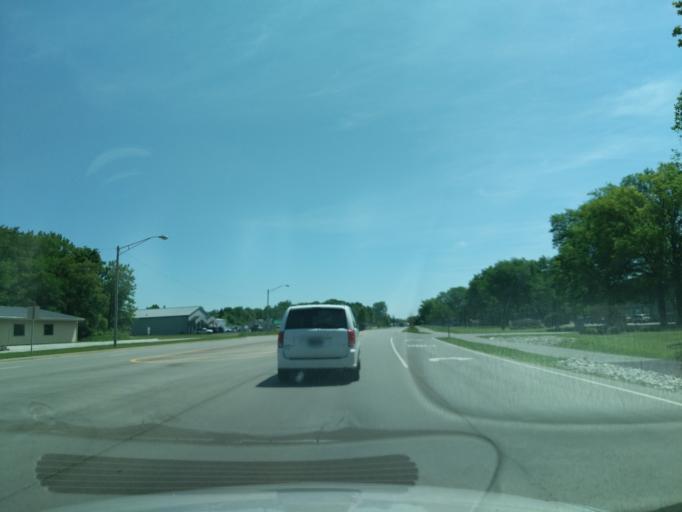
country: US
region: Indiana
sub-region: Huntington County
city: Huntington
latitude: 40.8923
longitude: -85.4867
